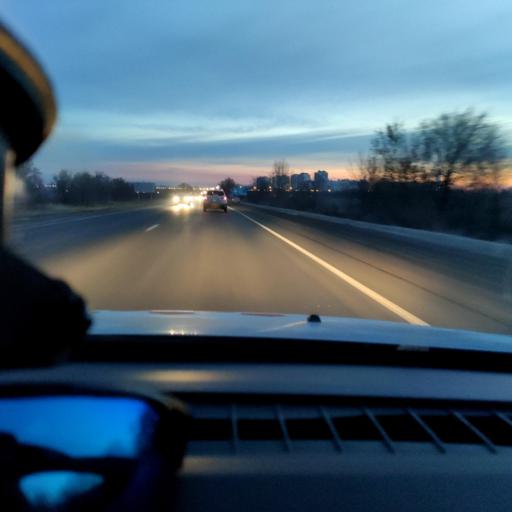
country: RU
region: Samara
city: Samara
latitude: 53.0870
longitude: 50.1444
